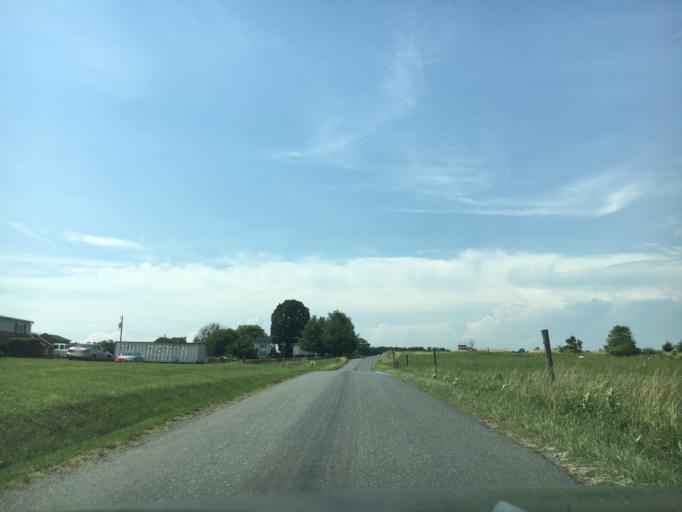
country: US
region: Virginia
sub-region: Pittsylvania County
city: Gretna
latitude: 36.9242
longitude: -79.4285
